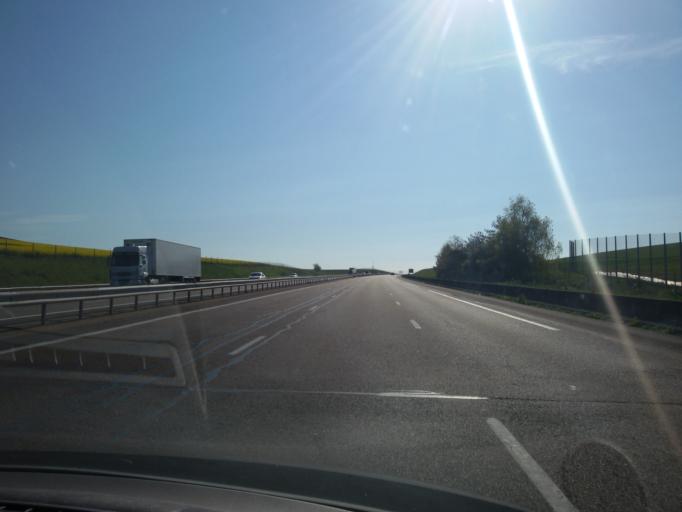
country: FR
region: Bourgogne
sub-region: Departement de l'Yonne
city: Aillant-sur-Tholon
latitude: 47.8977
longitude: 3.3783
